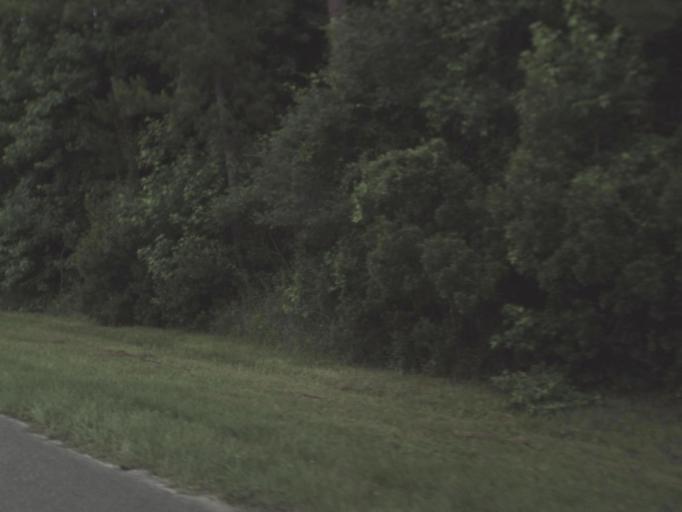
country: US
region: Florida
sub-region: Nassau County
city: Yulee
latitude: 30.6589
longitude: -81.6315
